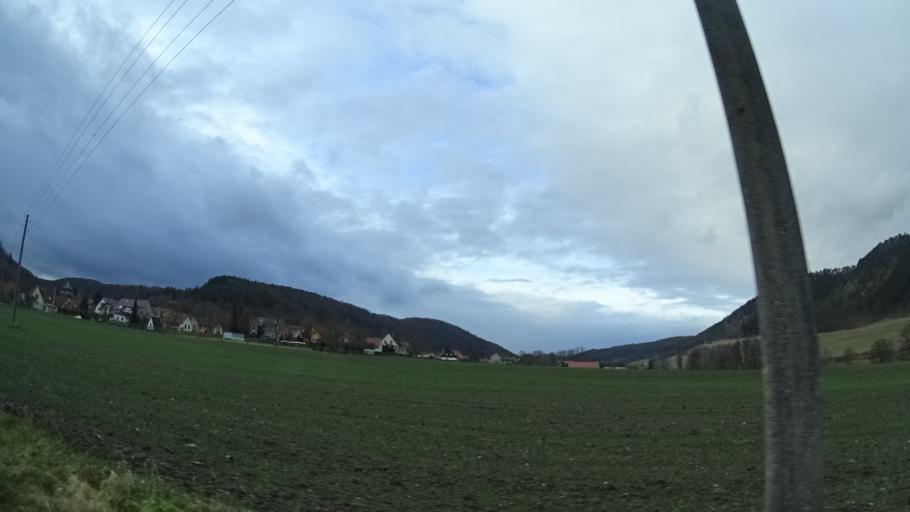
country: DE
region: Thuringia
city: Reinstadt
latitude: 50.8109
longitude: 11.4629
